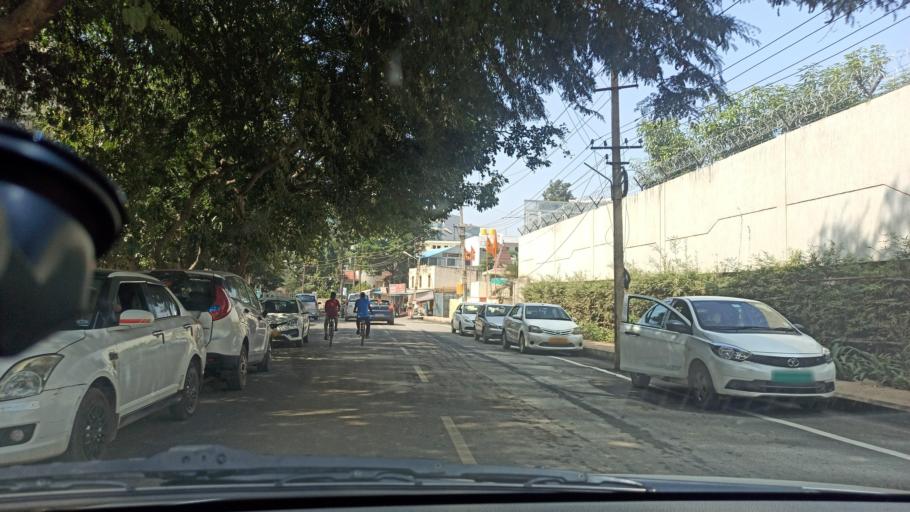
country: IN
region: Karnataka
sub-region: Bangalore Urban
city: Bangalore
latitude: 12.9401
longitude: 77.6927
